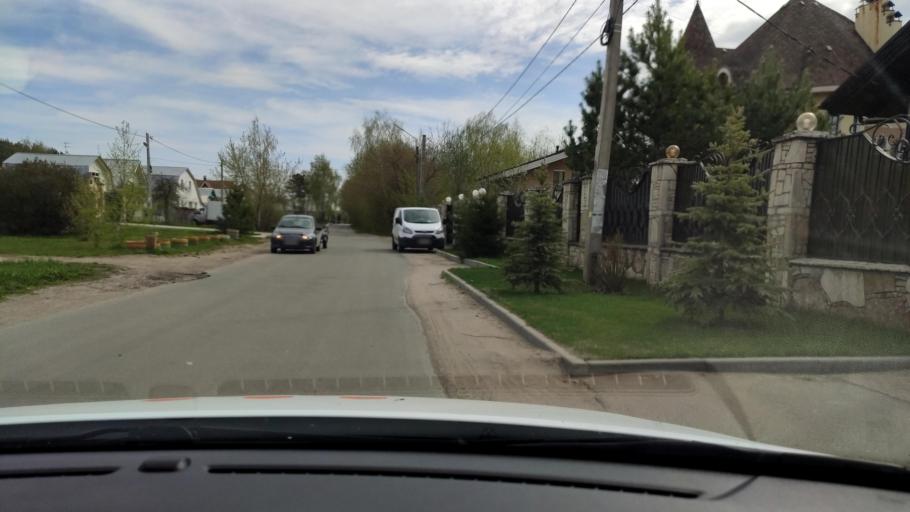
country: RU
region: Tatarstan
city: Osinovo
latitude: 55.8075
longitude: 48.8904
